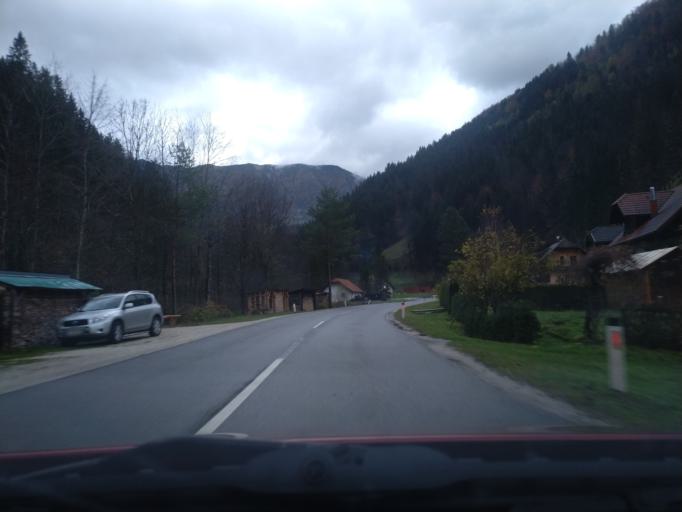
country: SI
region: Solcava
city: Solcava
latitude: 46.4078
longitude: 14.7016
